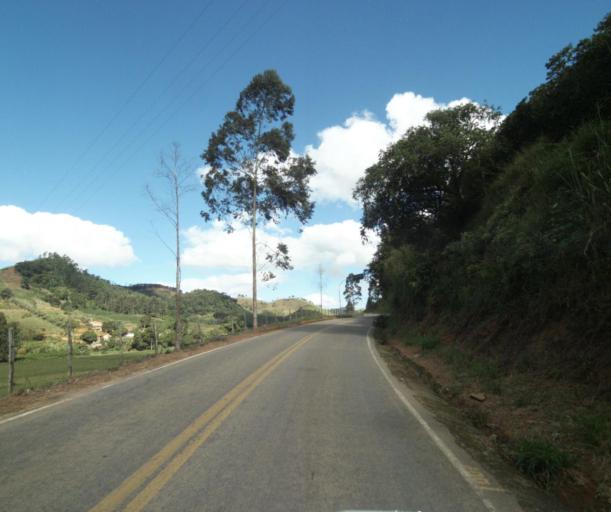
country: BR
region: Espirito Santo
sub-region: Irupi
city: Irupi
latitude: -20.5397
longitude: -41.6556
